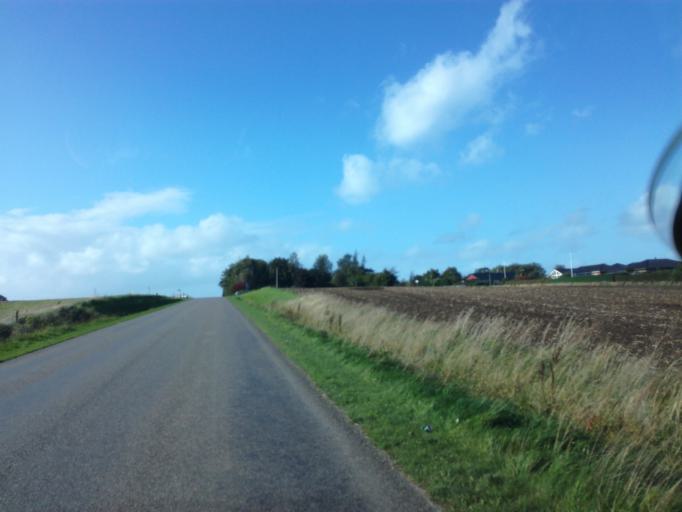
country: DK
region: South Denmark
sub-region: Vejle Kommune
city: Brejning
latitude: 55.6332
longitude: 9.7014
